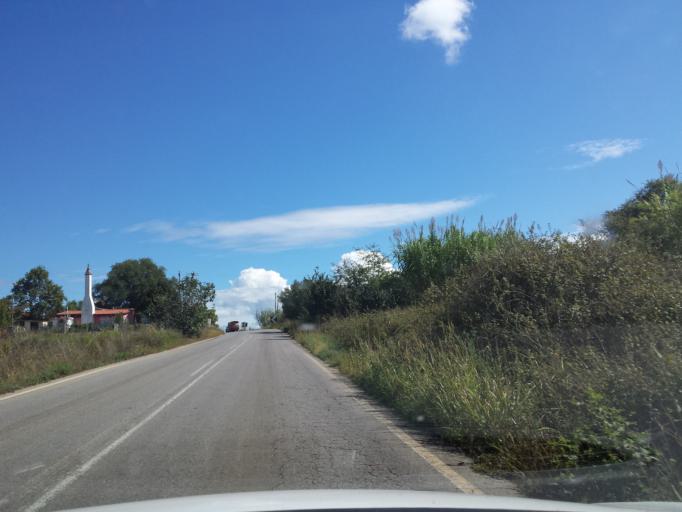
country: GR
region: Peloponnese
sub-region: Nomos Messinias
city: Vlakhopoulon
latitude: 36.9912
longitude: 21.8357
